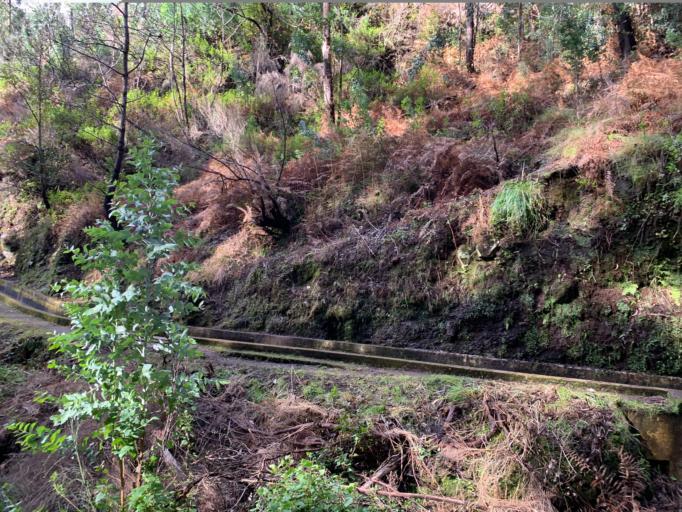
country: PT
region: Madeira
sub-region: Calheta
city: Estreito da Calheta
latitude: 32.7532
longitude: -17.1596
